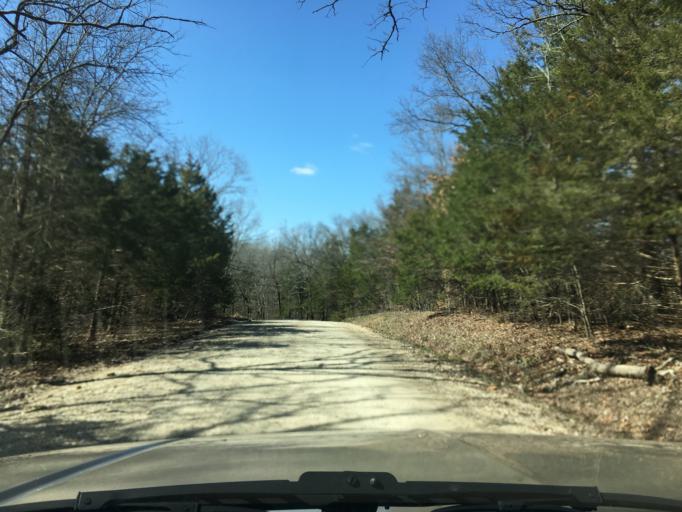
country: US
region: Missouri
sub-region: Franklin County
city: Gerald
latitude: 38.5199
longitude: -91.3197
